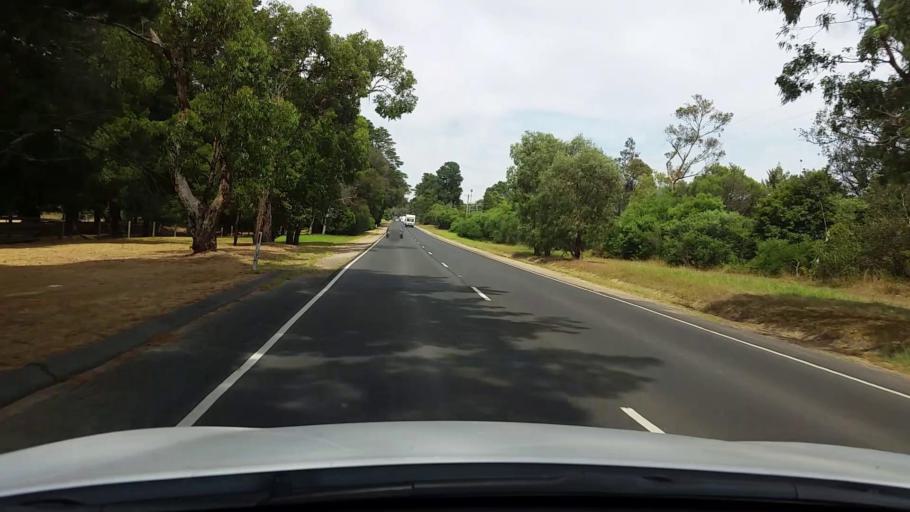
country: AU
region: Victoria
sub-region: Mornington Peninsula
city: Balnarring
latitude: -38.3686
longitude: 145.1344
